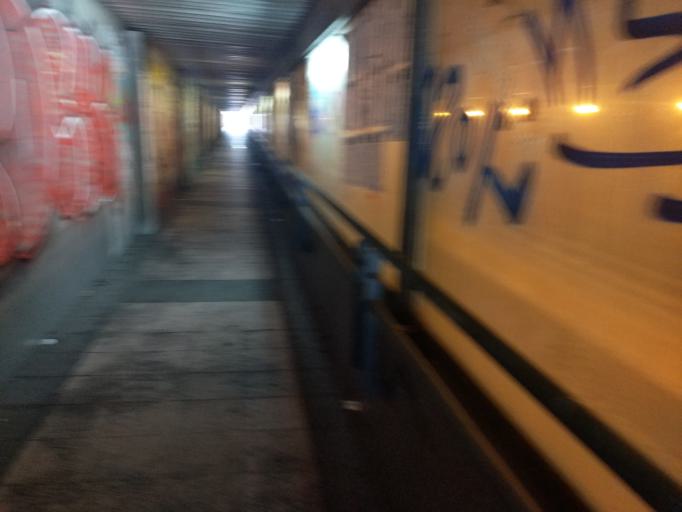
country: IT
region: Apulia
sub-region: Provincia di Bari
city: Bari
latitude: 41.1173
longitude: 16.8524
